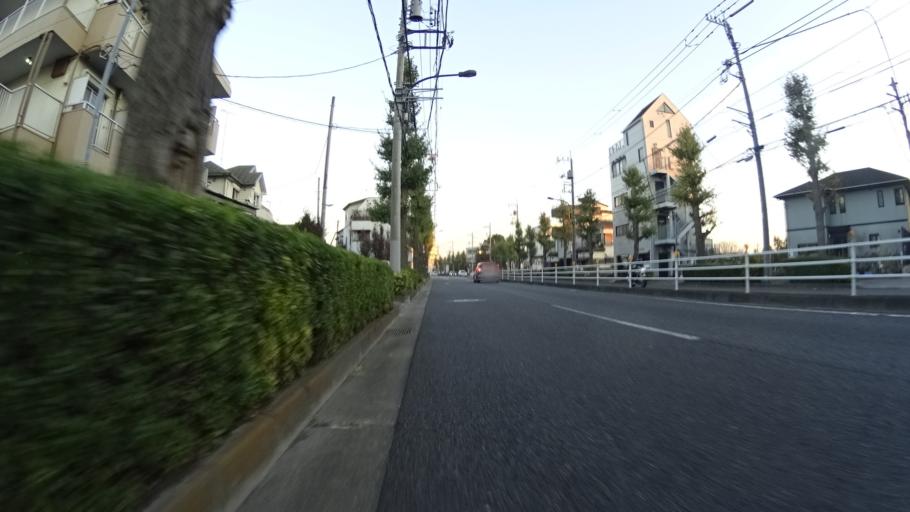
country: JP
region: Tokyo
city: Fussa
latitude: 35.7028
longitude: 139.3564
